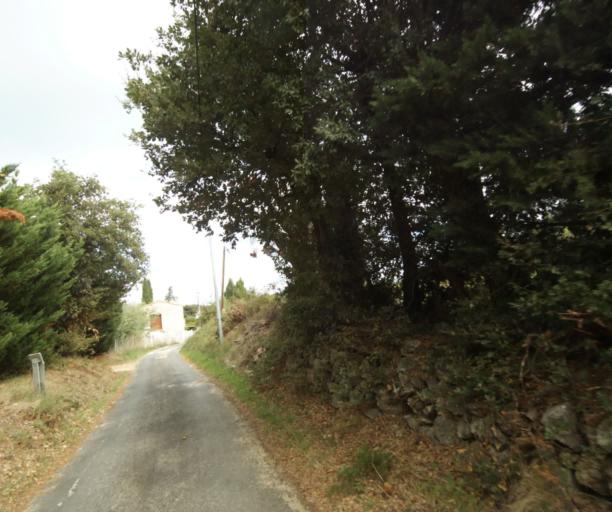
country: FR
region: Languedoc-Roussillon
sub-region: Departement des Pyrenees-Orientales
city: Argelers
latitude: 42.5361
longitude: 3.0430
